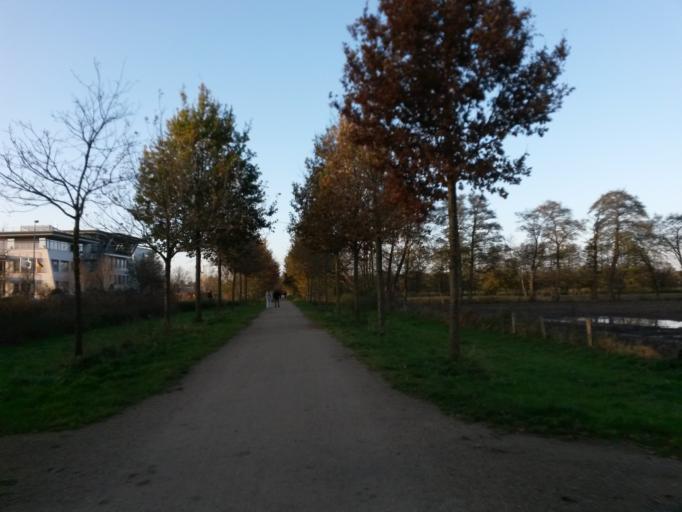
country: DE
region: Lower Saxony
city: Lilienthal
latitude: 53.0841
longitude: 8.9135
